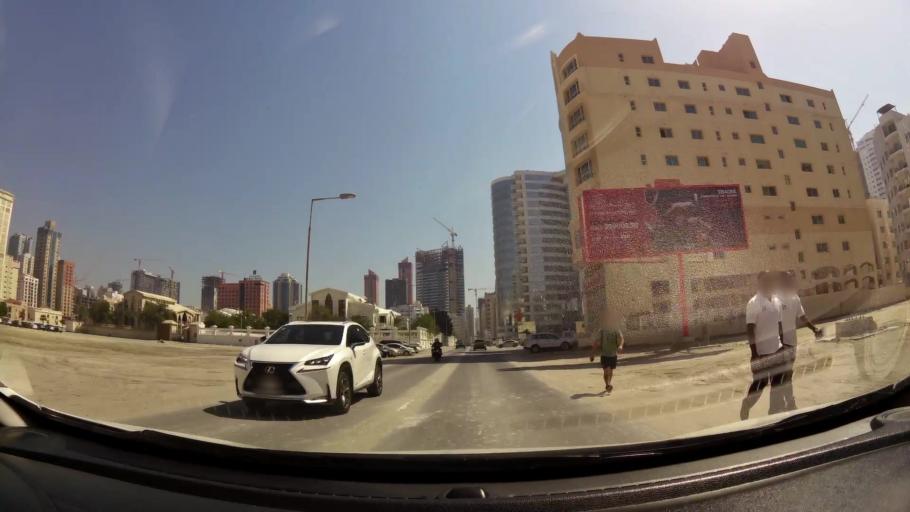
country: BH
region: Manama
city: Manama
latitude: 26.2153
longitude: 50.6041
